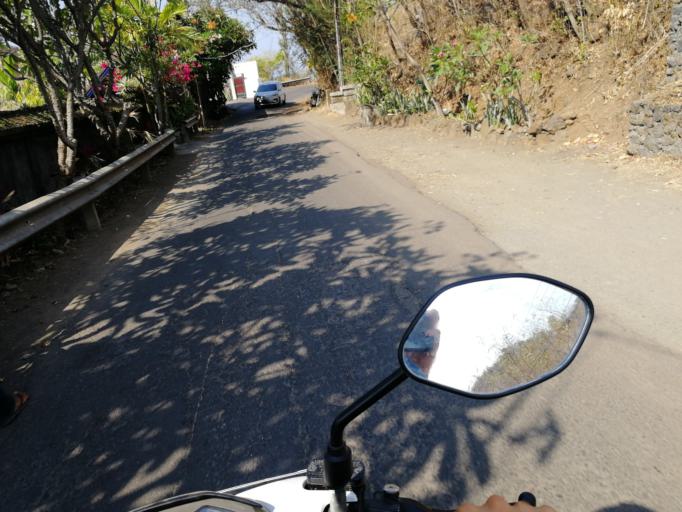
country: ID
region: Bali
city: Biaslantang Kaler
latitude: -8.3455
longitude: 115.6750
